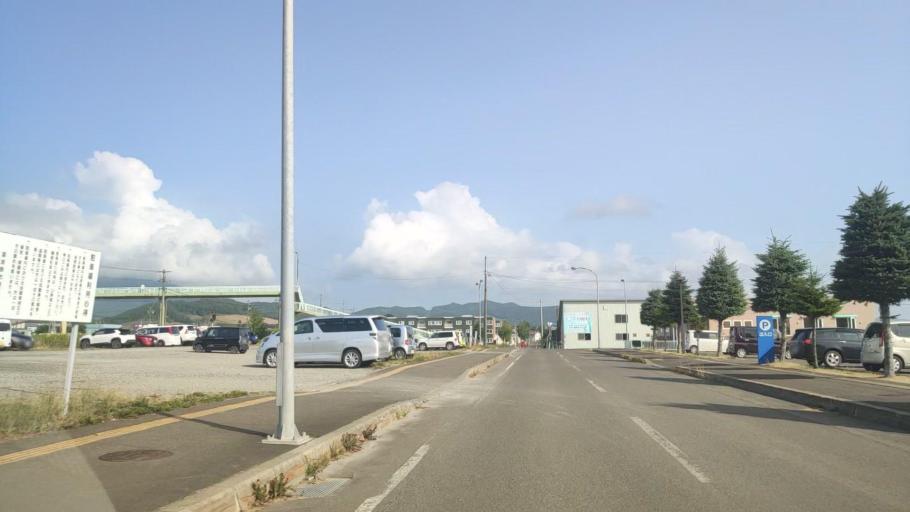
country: JP
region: Hokkaido
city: Shimo-furano
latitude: 43.3485
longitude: 142.3916
